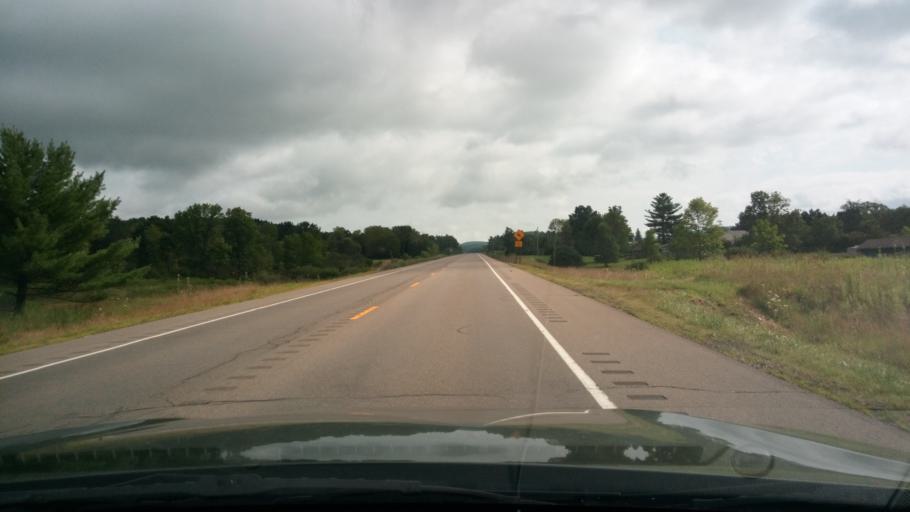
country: US
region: New York
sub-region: Chemung County
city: Horseheads North
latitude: 42.2005
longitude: -76.7815
